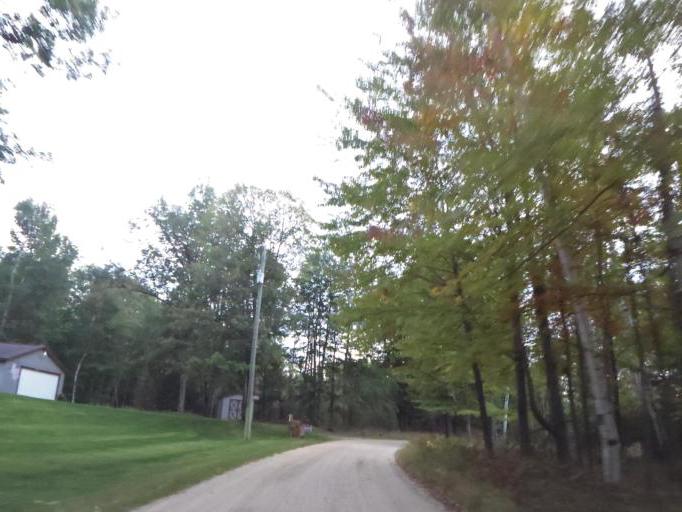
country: US
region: Michigan
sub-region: Roscommon County
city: Saint Helen
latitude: 44.3570
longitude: -84.4714
